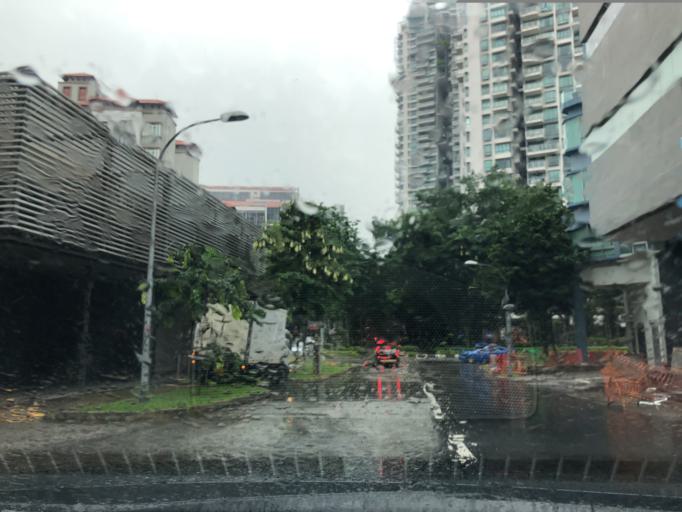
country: SG
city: Singapore
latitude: 1.2928
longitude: 103.8380
